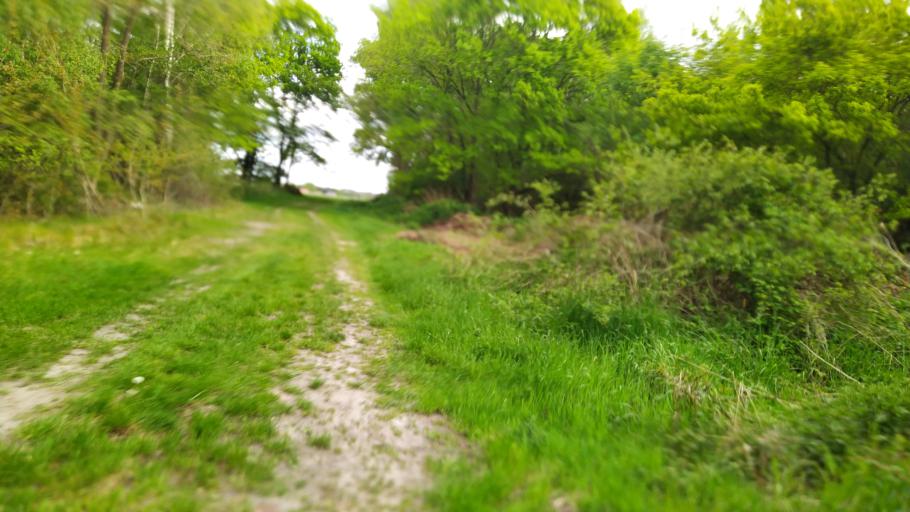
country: DE
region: Lower Saxony
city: Brest
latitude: 53.4293
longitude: 9.3909
